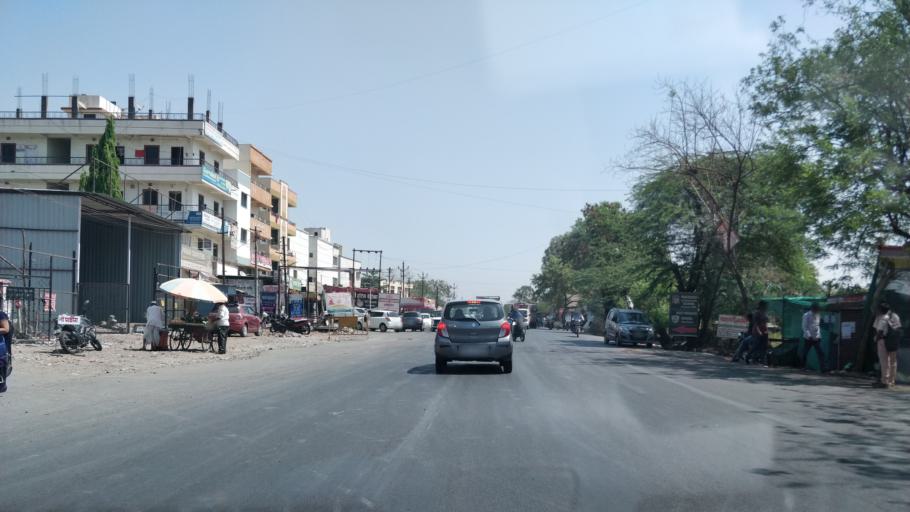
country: IN
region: Maharashtra
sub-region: Pune Division
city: Alandi
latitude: 18.6668
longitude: 73.8893
